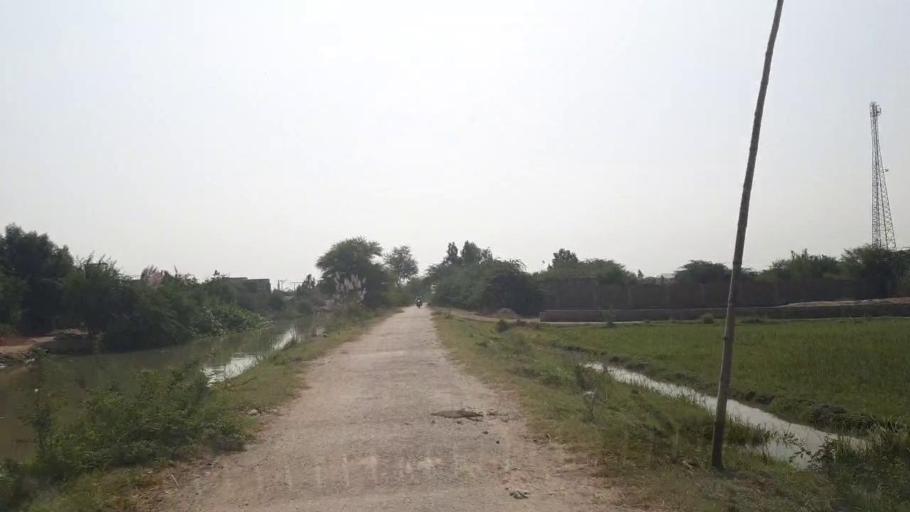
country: PK
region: Sindh
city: Badin
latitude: 24.6404
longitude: 68.8491
